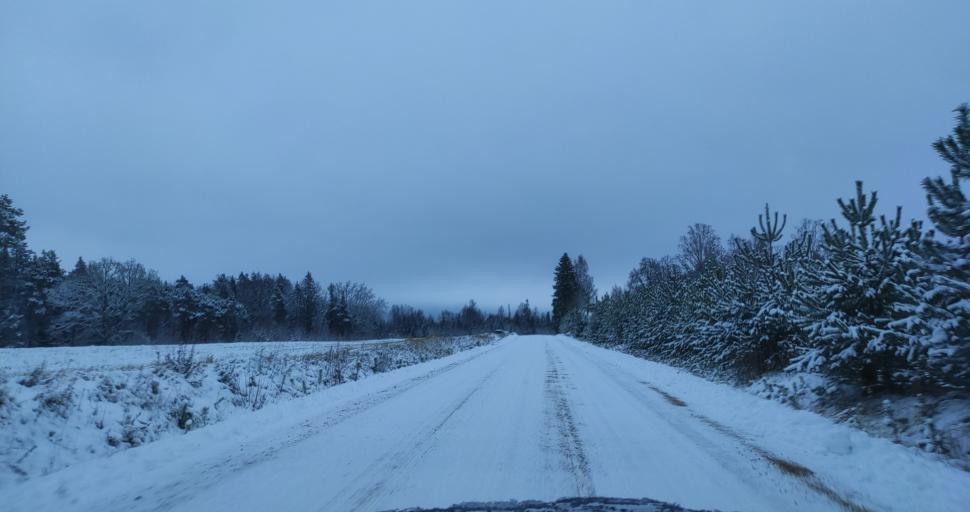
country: LV
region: Kuldigas Rajons
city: Kuldiga
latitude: 56.9513
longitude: 21.7673
